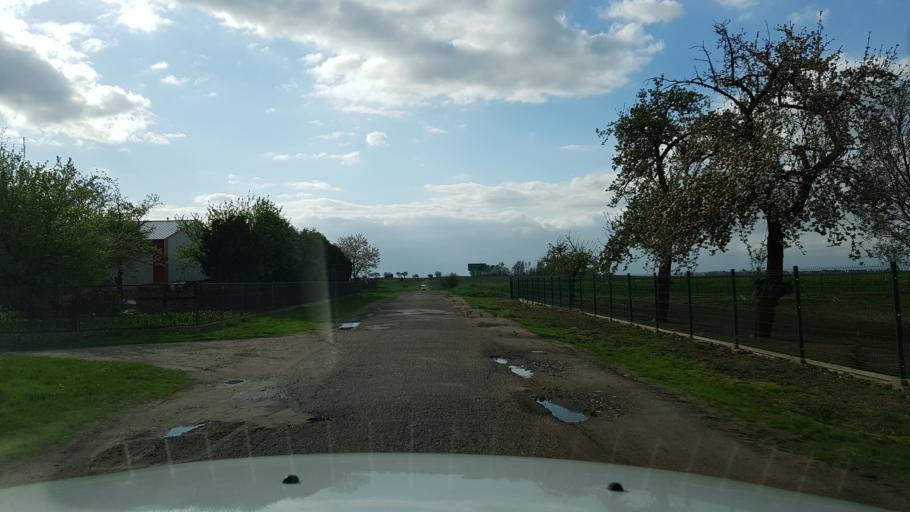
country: PL
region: West Pomeranian Voivodeship
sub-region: Powiat pyrzycki
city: Przelewice
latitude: 53.0757
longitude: 15.0943
